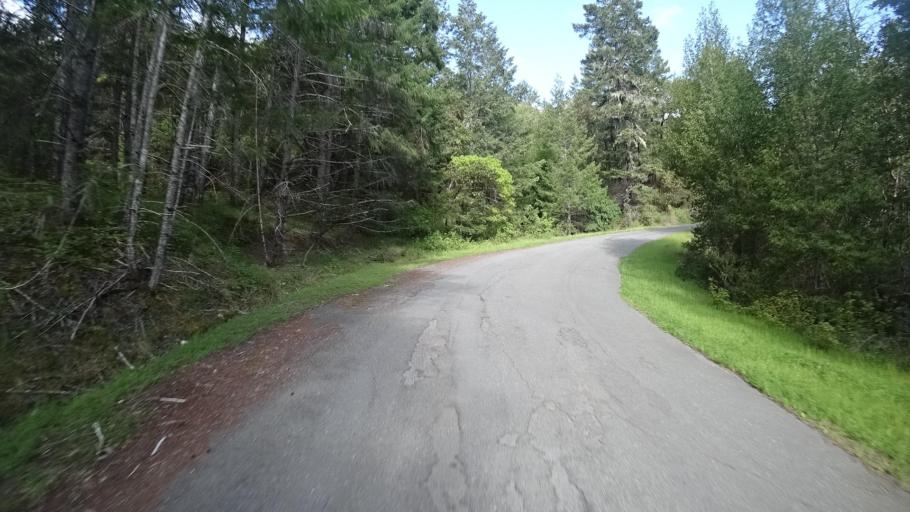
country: US
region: California
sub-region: Humboldt County
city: Redway
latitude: 40.2162
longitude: -123.6565
